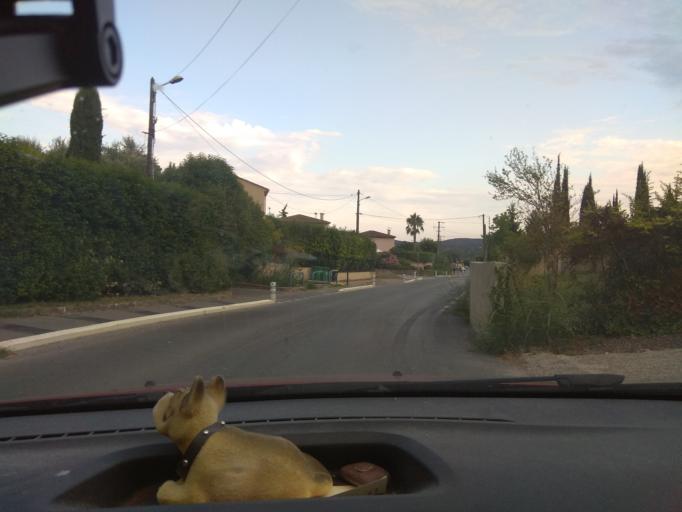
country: FR
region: Provence-Alpes-Cote d'Azur
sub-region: Departement des Alpes-Maritimes
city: La Colle-sur-Loup
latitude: 43.6816
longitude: 7.1065
